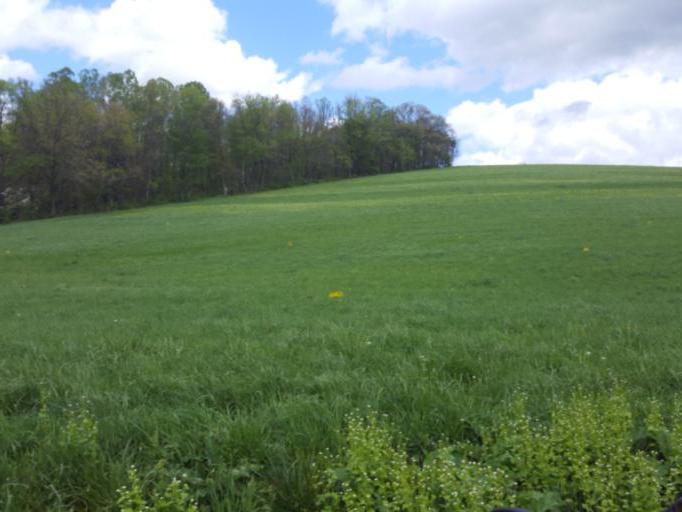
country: US
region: Ohio
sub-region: Ashland County
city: Loudonville
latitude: 40.5536
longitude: -82.2460
